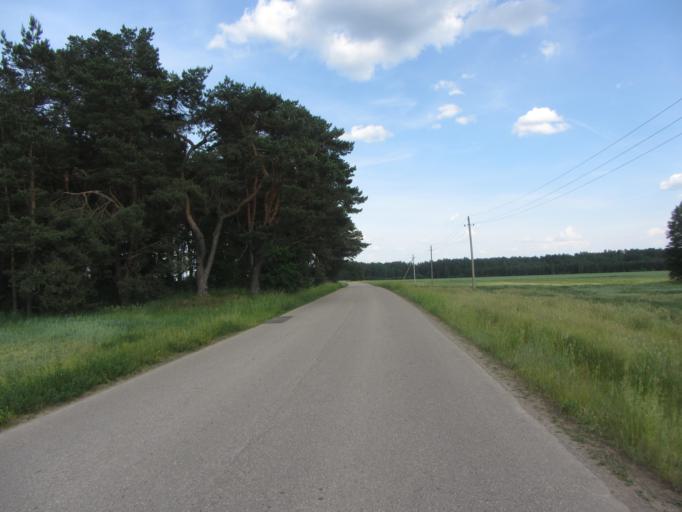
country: LT
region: Kauno apskritis
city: Jonava
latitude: 55.1416
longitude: 24.3654
